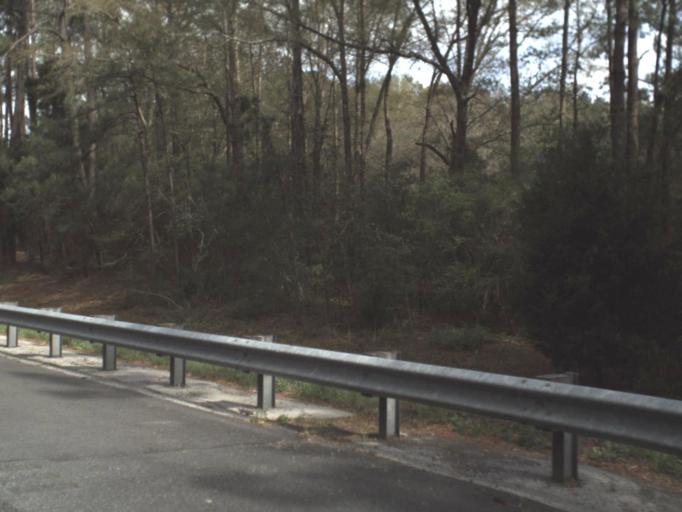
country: US
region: Florida
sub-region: Walton County
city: DeFuniak Springs
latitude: 30.6916
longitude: -86.0148
